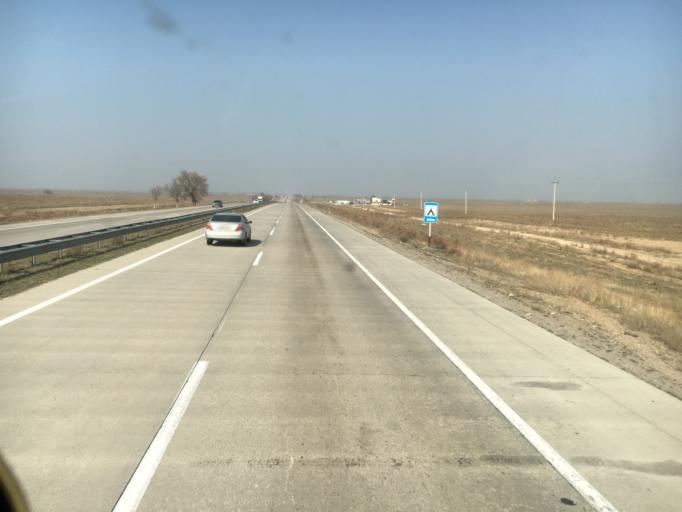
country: KZ
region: Ongtustik Qazaqstan
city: Temirlanovka
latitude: 42.8365
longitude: 69.1153
